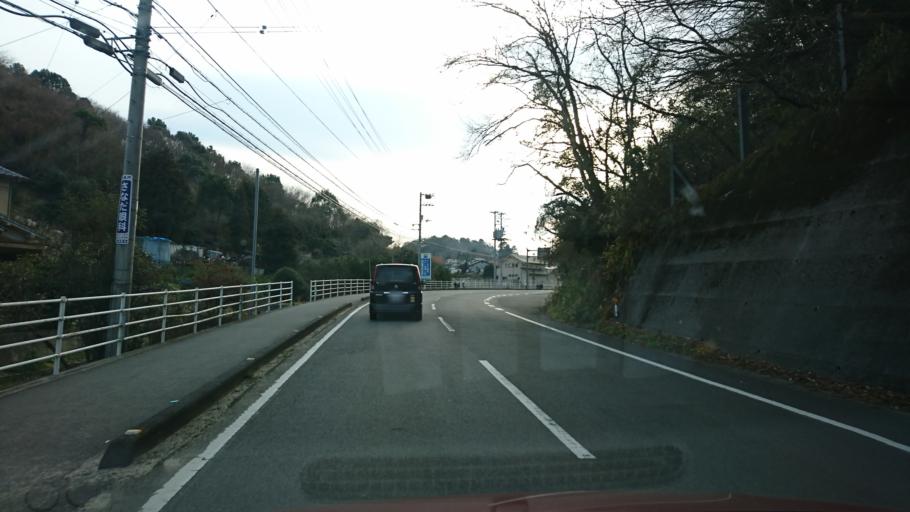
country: JP
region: Ehime
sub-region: Shikoku-chuo Shi
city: Matsuyama
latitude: 33.8751
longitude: 132.7946
